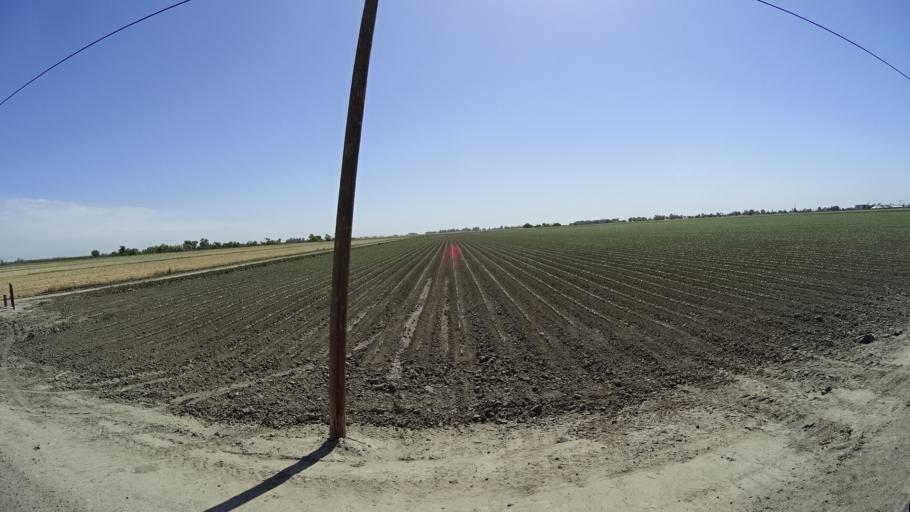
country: US
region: California
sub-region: Kings County
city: Stratford
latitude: 36.2031
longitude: -119.8340
